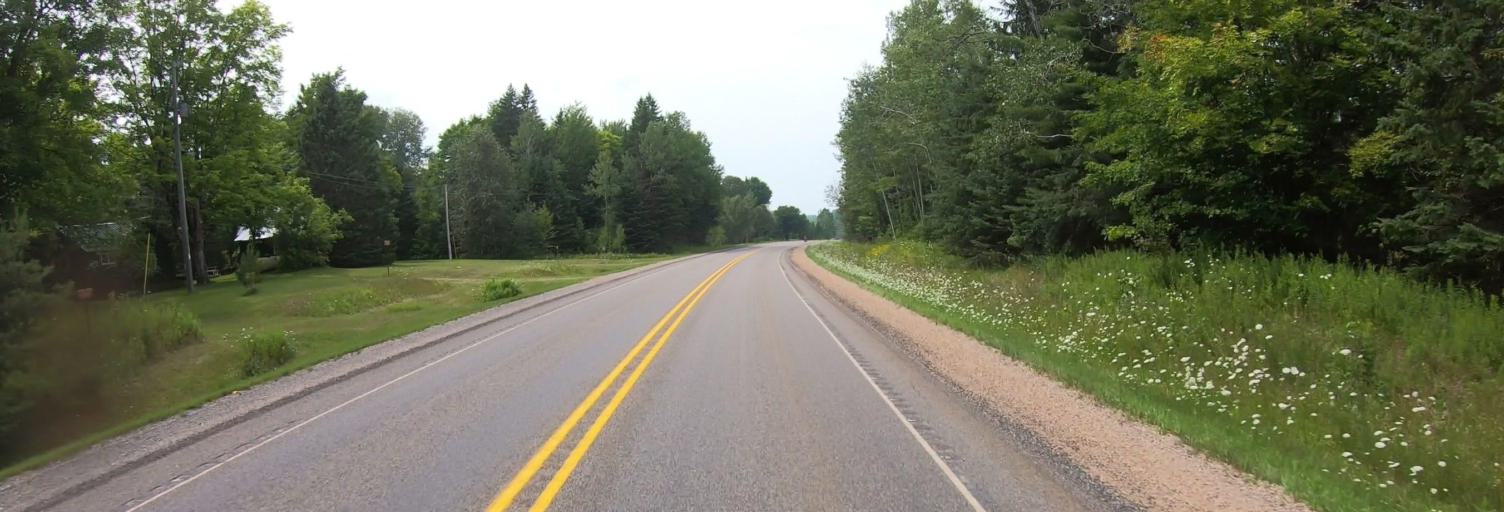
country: US
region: Michigan
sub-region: Alger County
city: Munising
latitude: 46.3324
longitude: -86.8411
